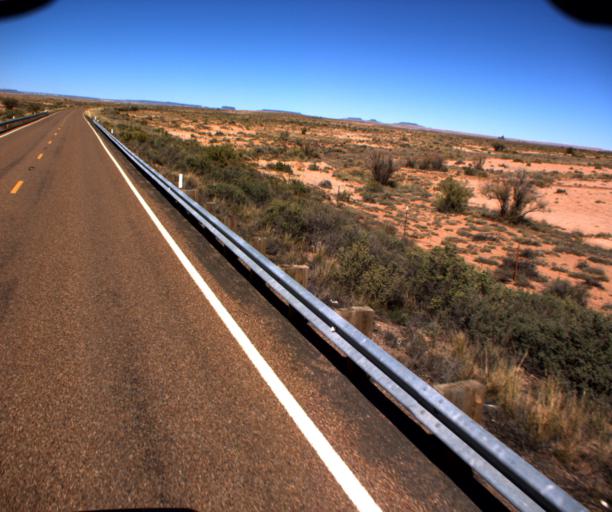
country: US
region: Arizona
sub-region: Navajo County
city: Holbrook
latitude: 35.0501
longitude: -110.0949
